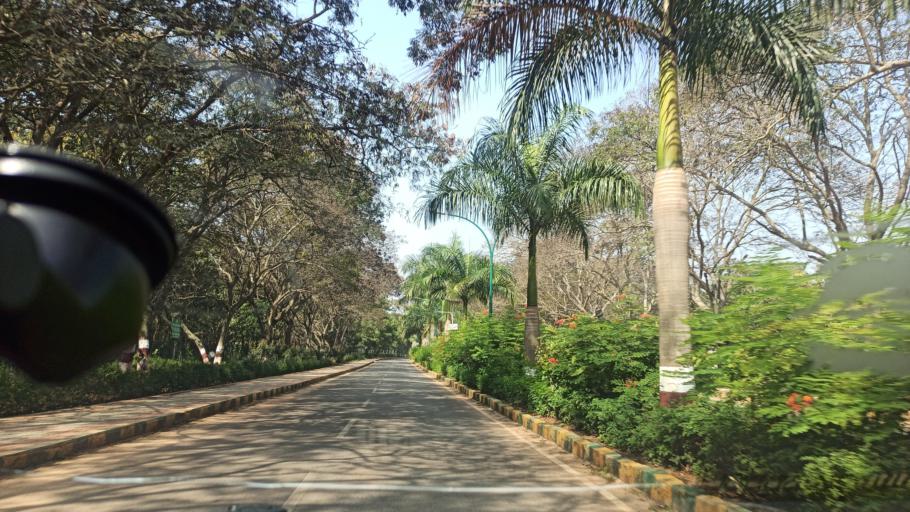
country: IN
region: Karnataka
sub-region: Bangalore Urban
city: Yelahanka
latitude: 13.0748
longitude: 77.5867
